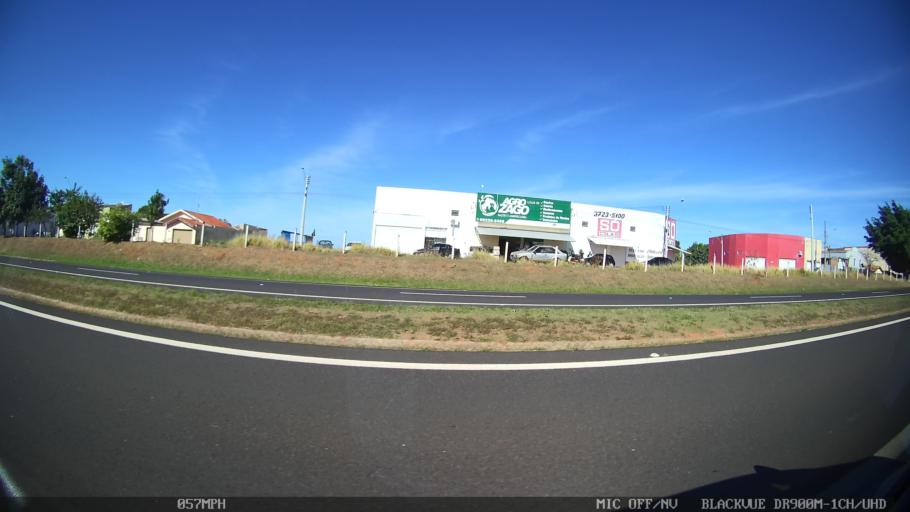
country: BR
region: Sao Paulo
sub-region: Franca
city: Franca
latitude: -20.5739
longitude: -47.3704
